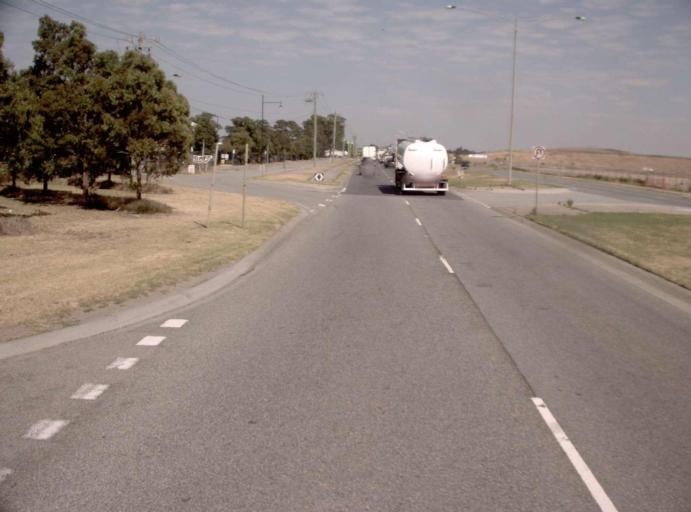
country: AU
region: Victoria
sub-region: Greater Dandenong
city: Dandenong
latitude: -38.0132
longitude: 145.2014
